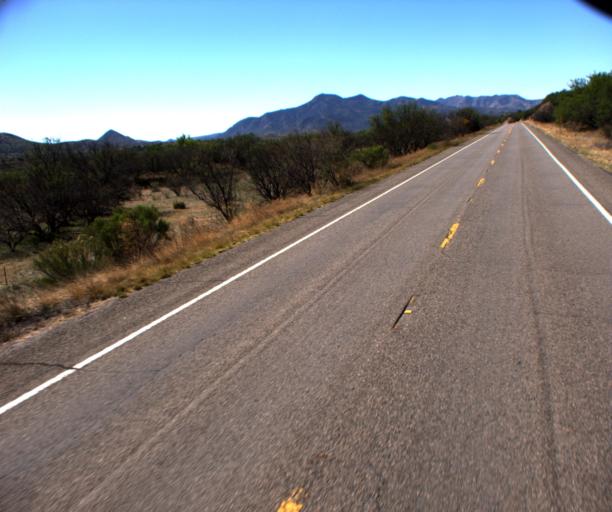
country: US
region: Arizona
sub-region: Santa Cruz County
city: Rio Rico
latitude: 31.5945
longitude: -110.7248
